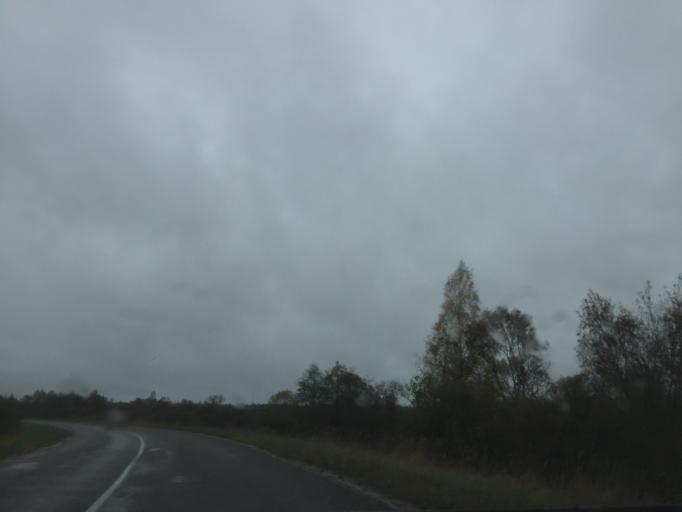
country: LV
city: Tireli
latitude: 56.8268
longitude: 23.5678
